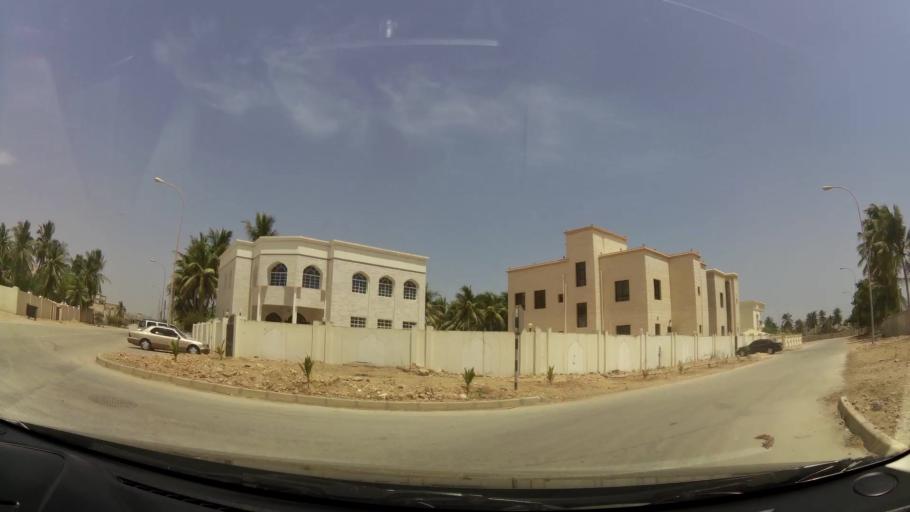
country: OM
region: Zufar
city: Salalah
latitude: 17.0650
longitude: 54.1510
